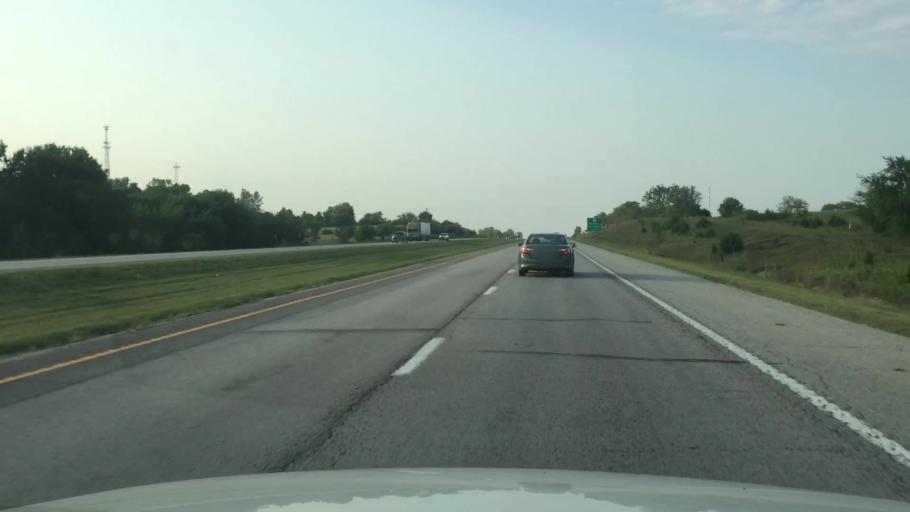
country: US
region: Missouri
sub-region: Harrison County
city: Bethany
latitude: 40.2426
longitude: -94.0127
